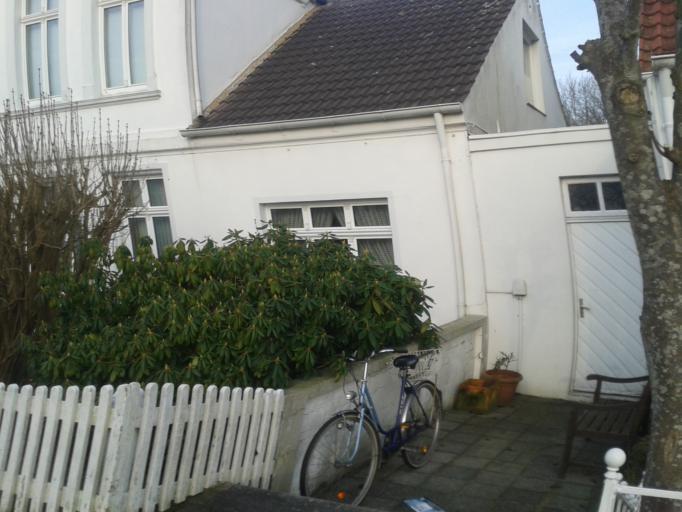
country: DE
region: Lower Saxony
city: Norderney
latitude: 53.7045
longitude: 7.1485
